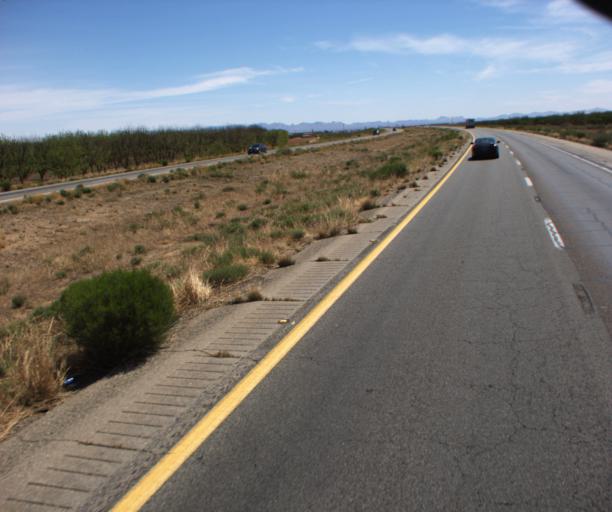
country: US
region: Arizona
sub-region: Cochise County
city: Willcox
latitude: 32.3181
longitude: -109.4923
